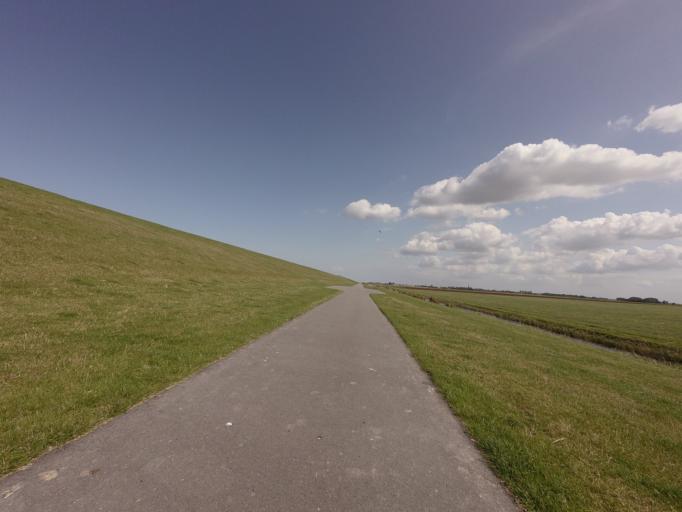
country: NL
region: Friesland
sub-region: Gemeente Dongeradeel
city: Holwerd
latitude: 53.3709
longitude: 5.8604
